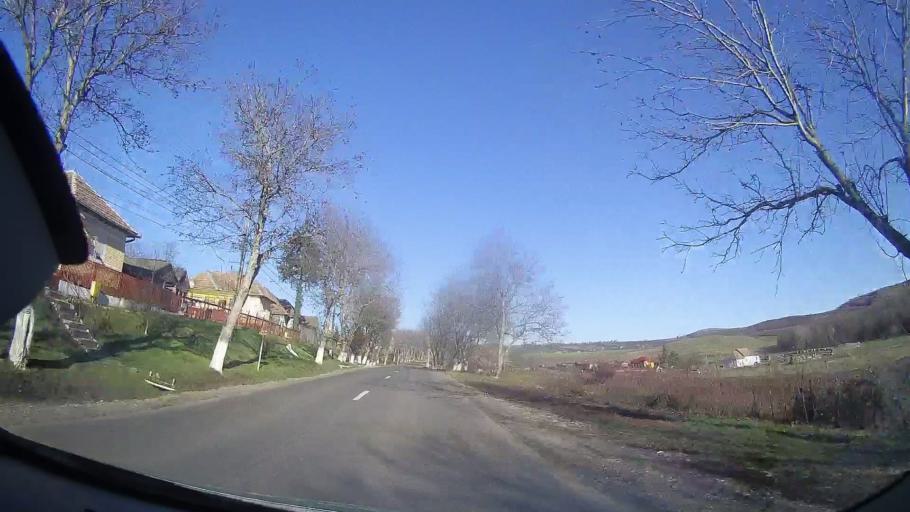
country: RO
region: Mures
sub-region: Comuna Sarmasu
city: Balda
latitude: 46.7336
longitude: 24.1475
